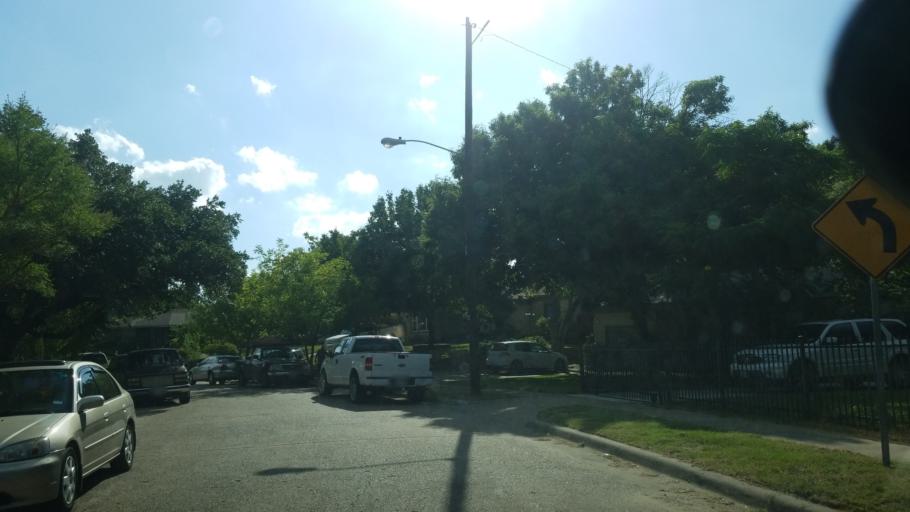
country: US
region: Texas
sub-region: Dallas County
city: Dallas
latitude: 32.7667
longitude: -96.7154
